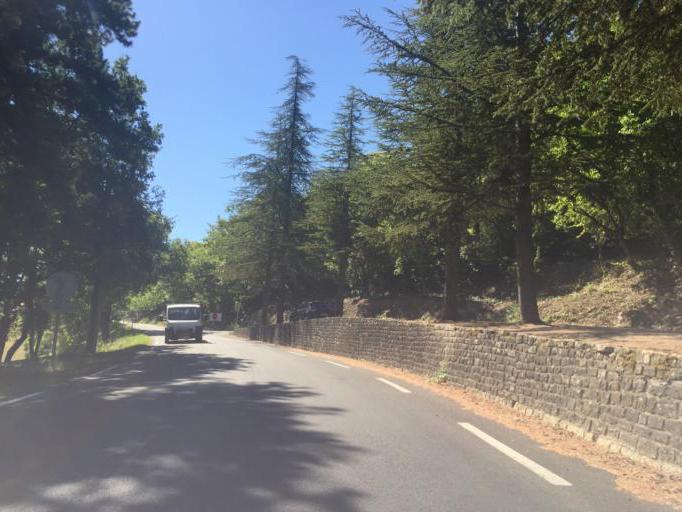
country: FR
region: Provence-Alpes-Cote d'Azur
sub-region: Departement du Vaucluse
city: Venasque
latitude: 44.0000
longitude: 5.1446
